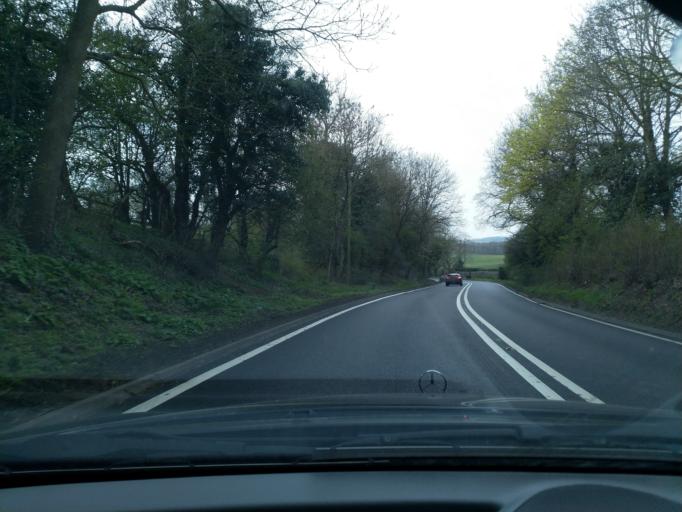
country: GB
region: England
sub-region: Warwickshire
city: Stratford-upon-Avon
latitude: 52.2295
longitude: -1.6605
